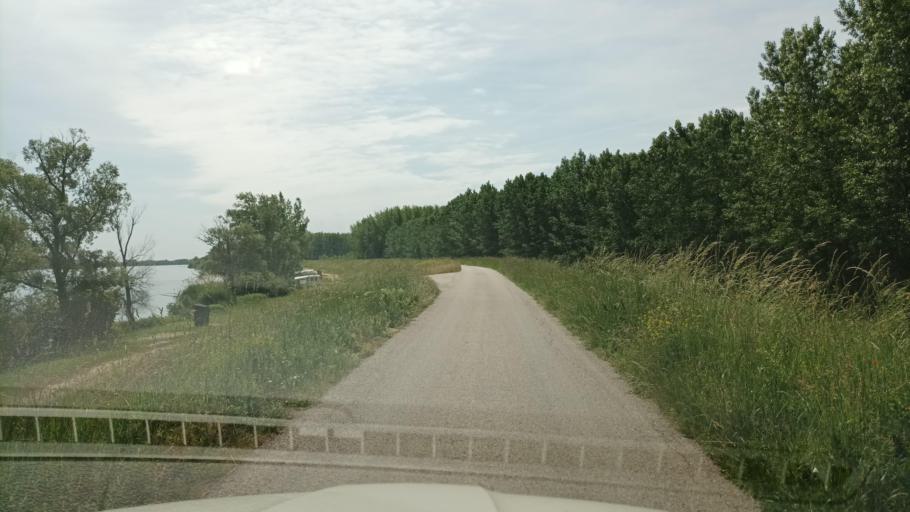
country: HU
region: Fejer
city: Racalmas
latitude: 47.0563
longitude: 18.9554
